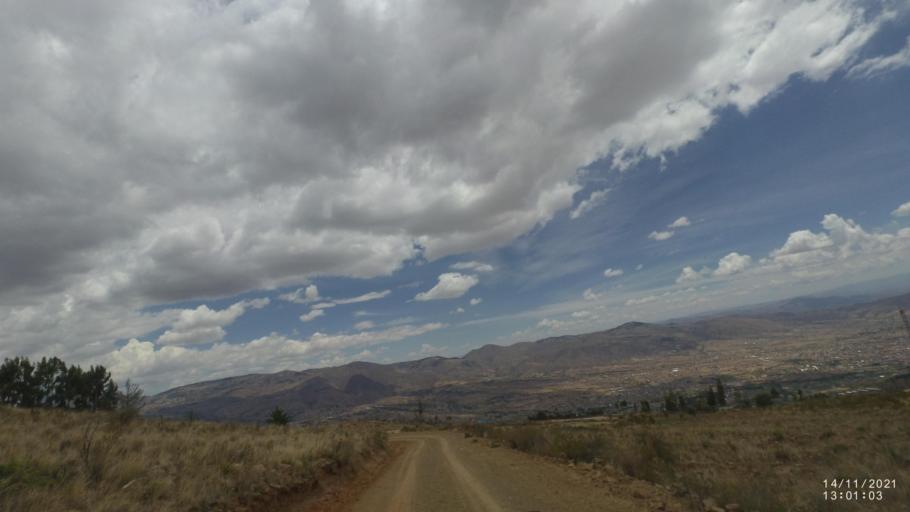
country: BO
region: Cochabamba
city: Colomi
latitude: -17.3656
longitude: -65.9764
